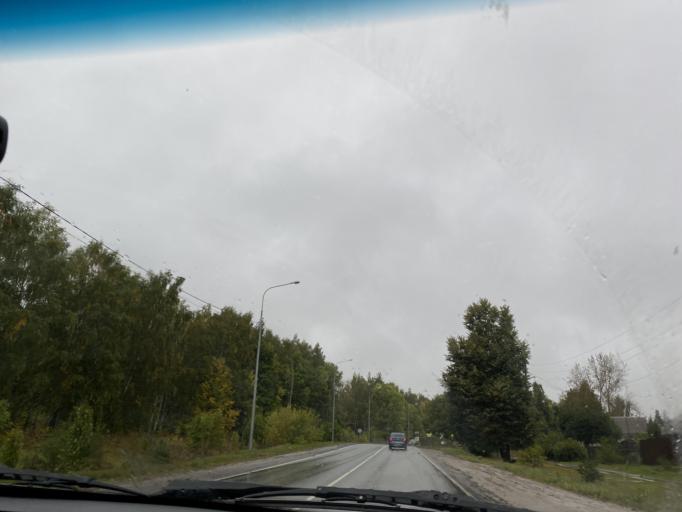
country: RU
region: Rjazan
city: Starozhilovo
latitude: 54.4442
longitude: 39.8905
